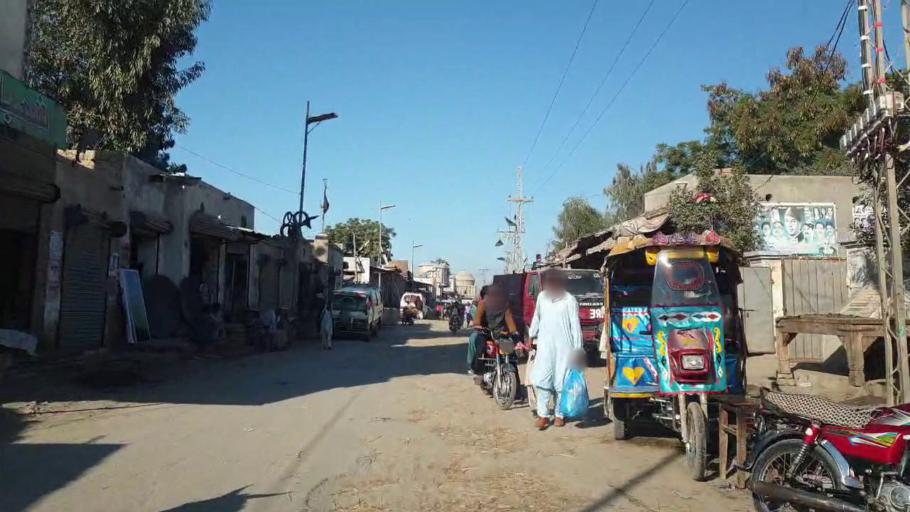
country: PK
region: Sindh
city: New Badah
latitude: 27.3314
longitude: 68.0187
